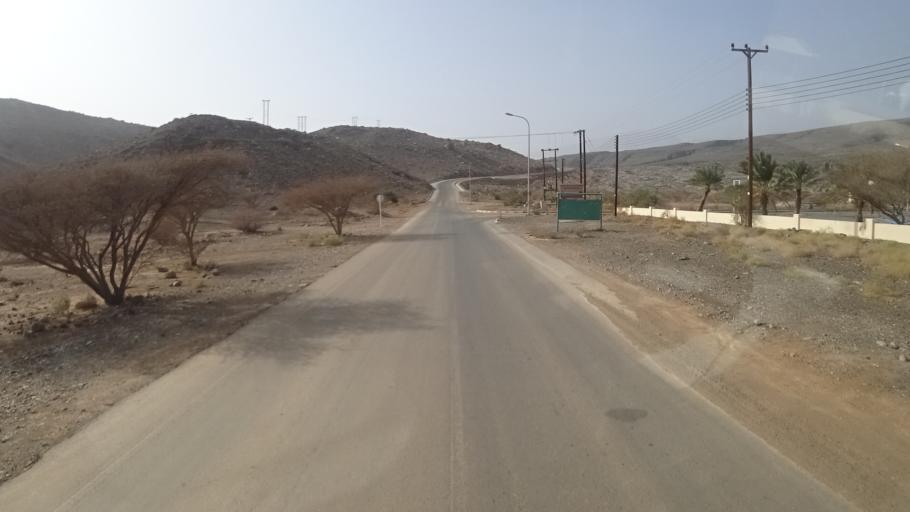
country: OM
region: Muhafazat ad Dakhiliyah
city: Bahla'
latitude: 23.0686
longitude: 57.3680
